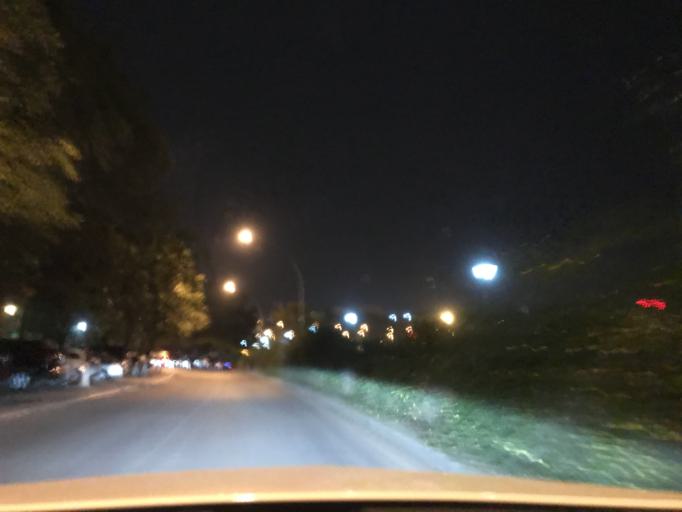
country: CN
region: Sichuan
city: Mianyang
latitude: 31.4490
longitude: 104.7498
